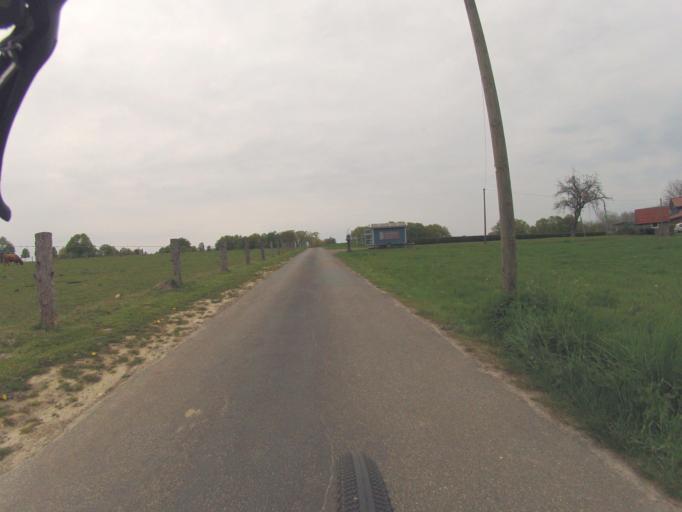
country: DE
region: North Rhine-Westphalia
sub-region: Regierungsbezirk Munster
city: Westerkappeln
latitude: 52.3028
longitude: 7.8448
